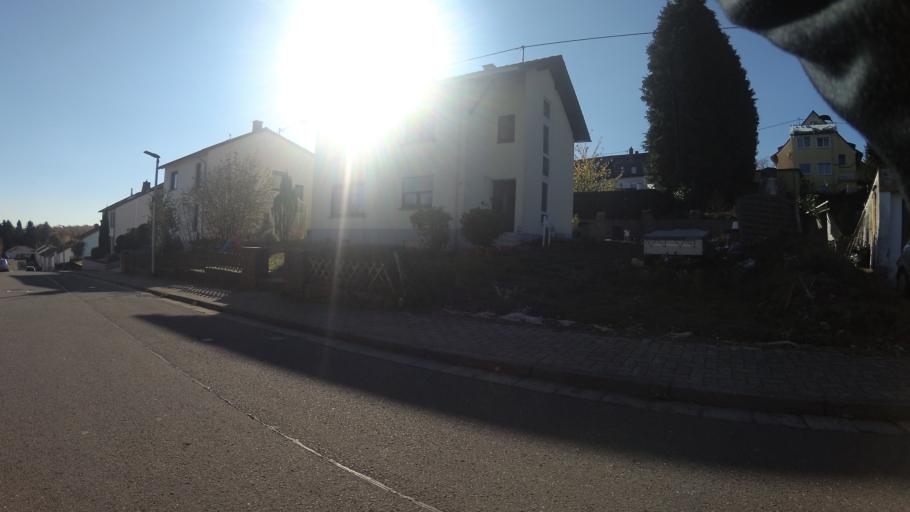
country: DE
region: Saarland
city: Bexbach
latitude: 49.3419
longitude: 7.2183
